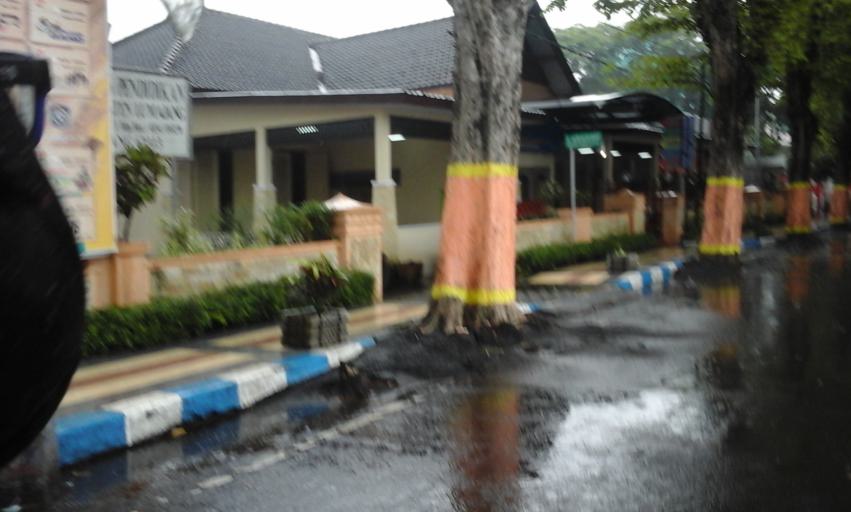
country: ID
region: East Java
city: Lumajang
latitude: -8.1357
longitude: 113.2231
